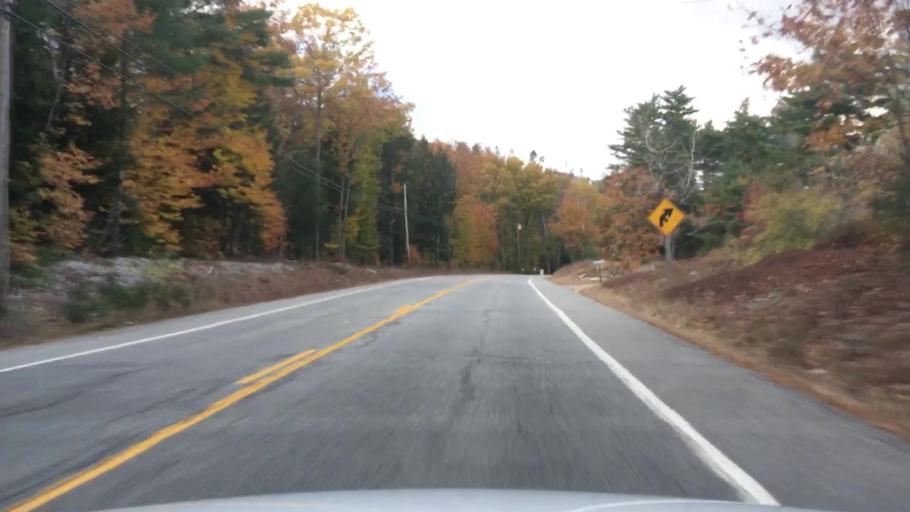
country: US
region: Maine
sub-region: Androscoggin County
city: Livermore
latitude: 44.3855
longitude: -70.2555
